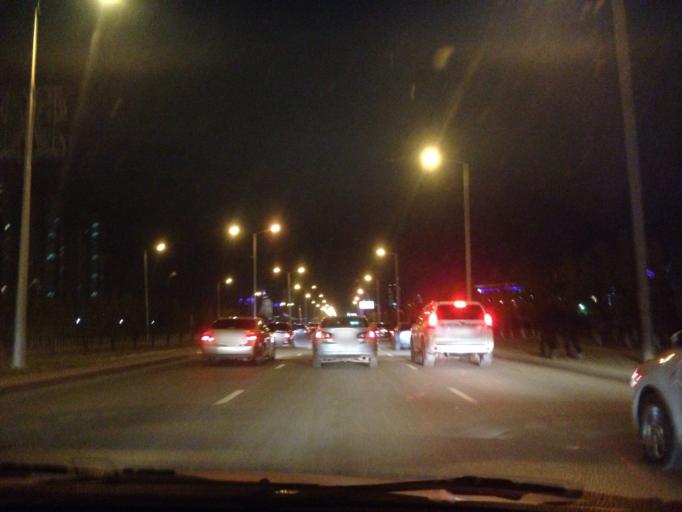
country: KZ
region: Astana Qalasy
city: Astana
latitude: 51.1147
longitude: 71.4003
